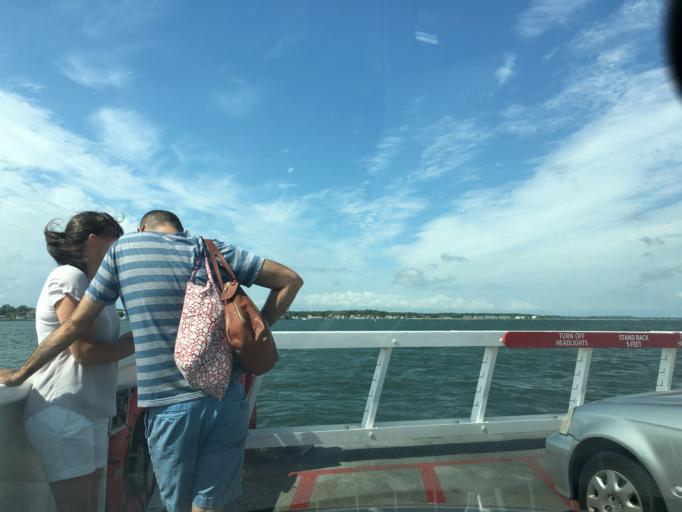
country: US
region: New York
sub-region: Suffolk County
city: Greenport
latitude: 41.0948
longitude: -72.3580
